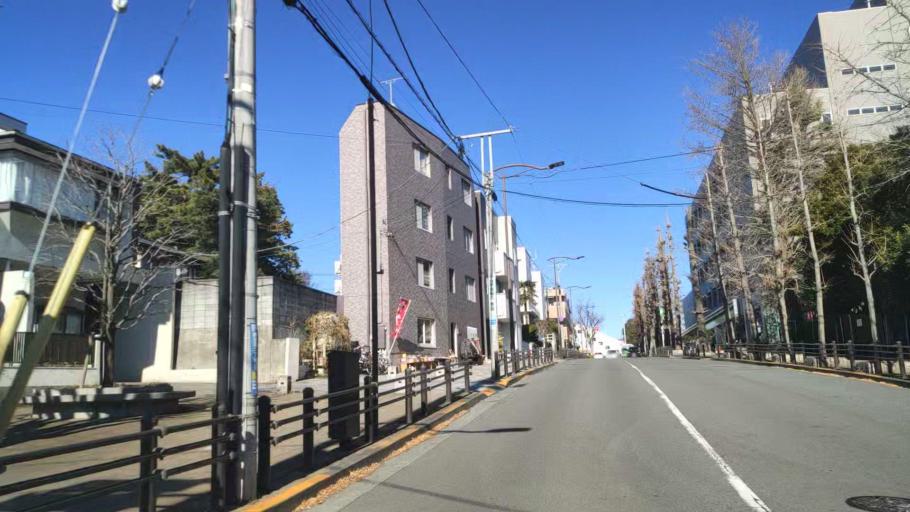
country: JP
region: Tokyo
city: Musashino
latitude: 35.7270
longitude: 139.5634
